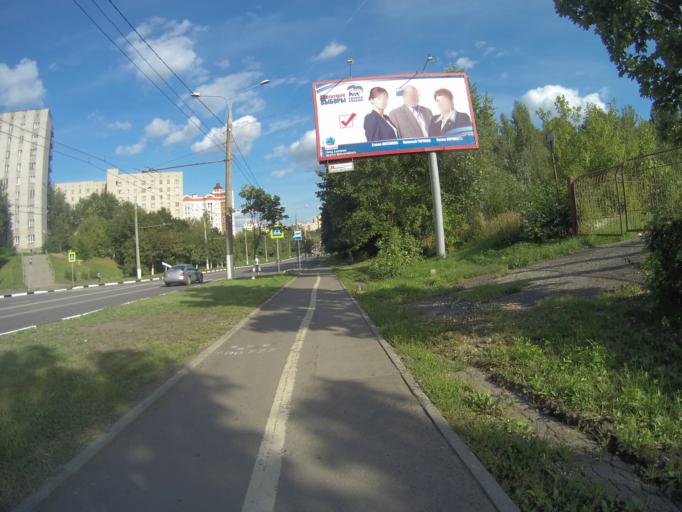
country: RU
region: Vladimir
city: Vladimir
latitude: 56.1404
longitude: 40.3724
